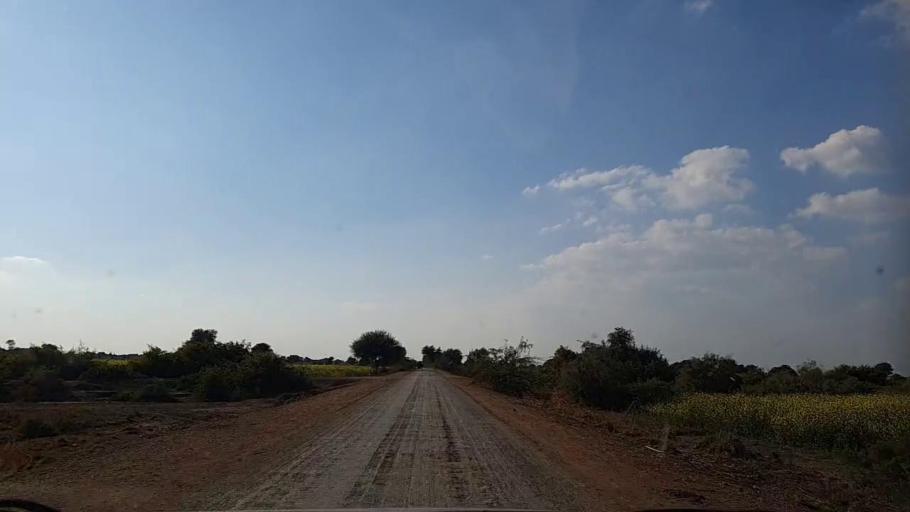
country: PK
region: Sindh
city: Pithoro
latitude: 25.6492
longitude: 69.2971
